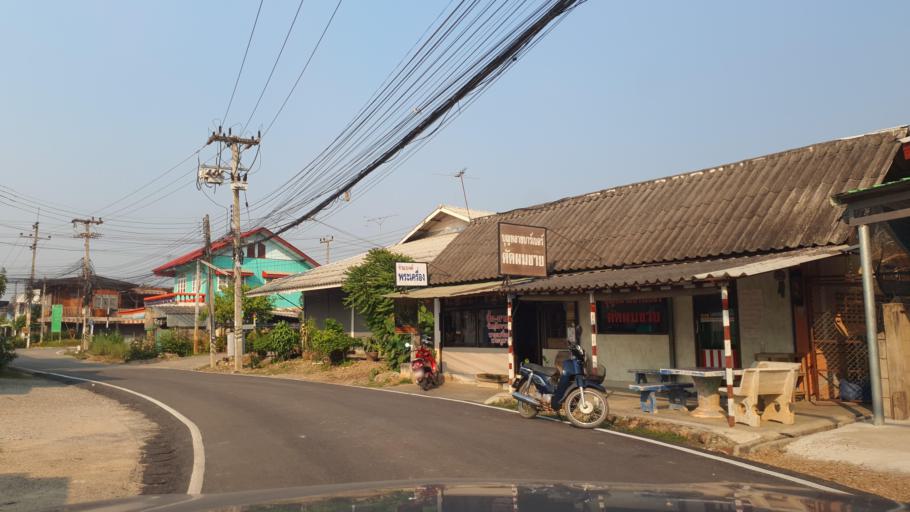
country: TH
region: Chiang Mai
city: Mae Taeng
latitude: 19.1447
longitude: 99.0122
